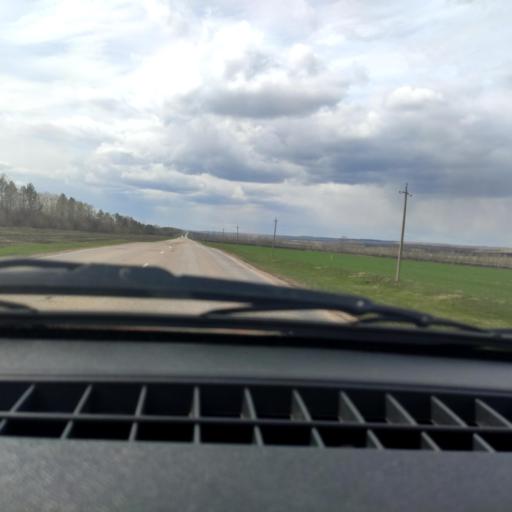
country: RU
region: Bashkortostan
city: Chekmagush
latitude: 55.1086
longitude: 54.9589
